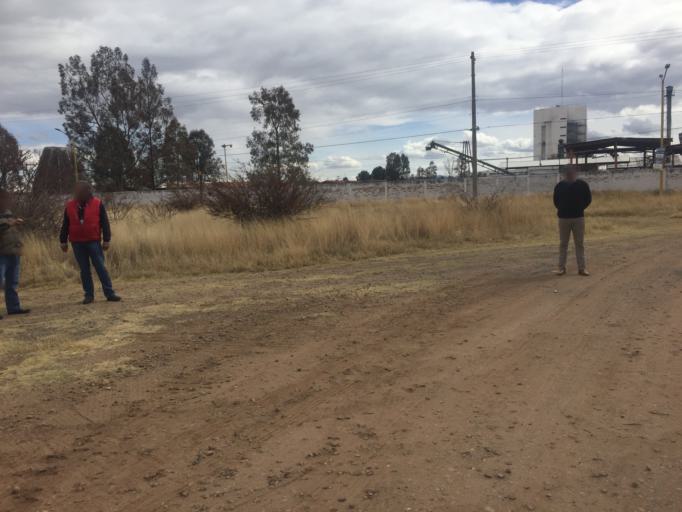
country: MX
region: Durango
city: Victoria de Durango
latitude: 24.0671
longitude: -104.6056
